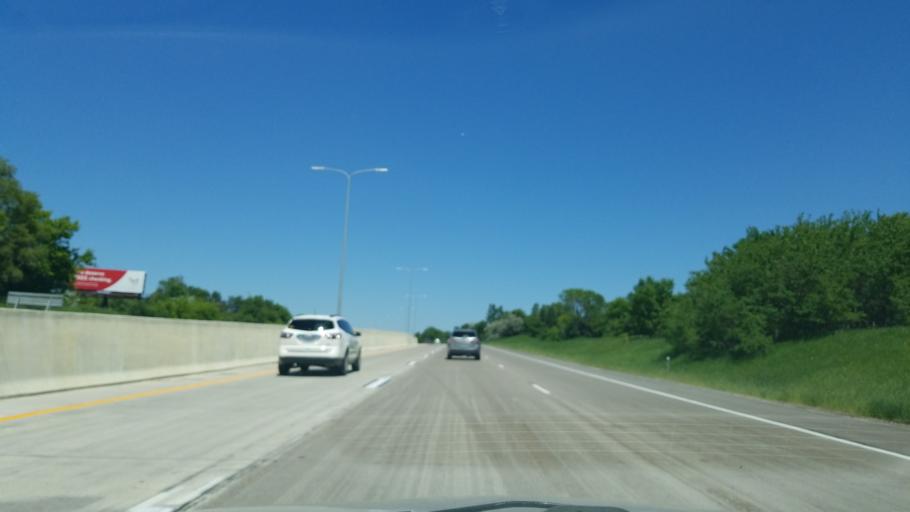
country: US
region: Minnesota
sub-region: Ramsey County
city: Vadnais Heights
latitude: 45.0720
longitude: -93.0532
